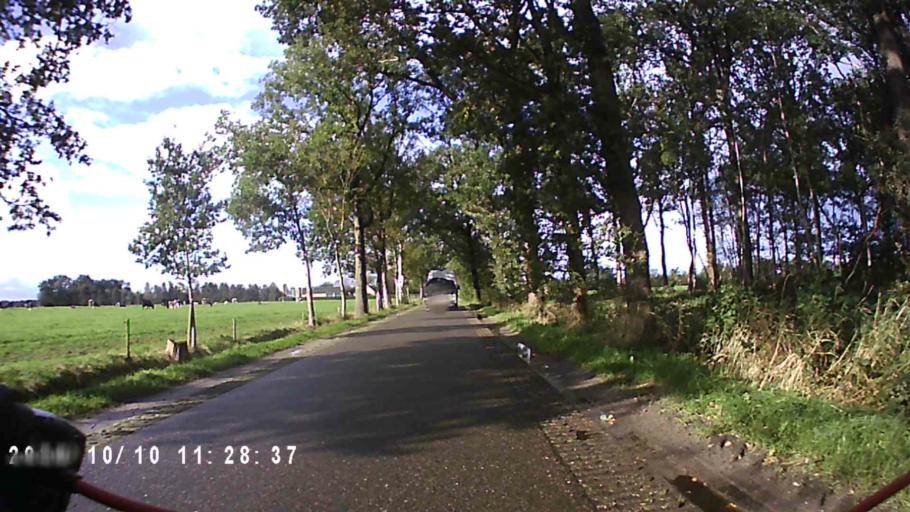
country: NL
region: Friesland
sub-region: Gemeente Smallingerland
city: Drachtstercompagnie
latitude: 53.0869
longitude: 6.1524
